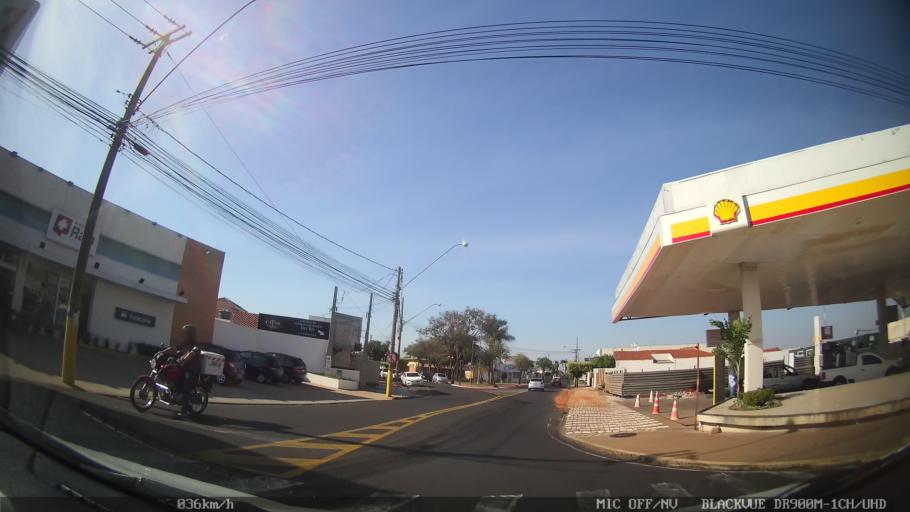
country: BR
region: Sao Paulo
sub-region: Sao Jose Do Rio Preto
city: Sao Jose do Rio Preto
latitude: -20.8086
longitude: -49.3966
